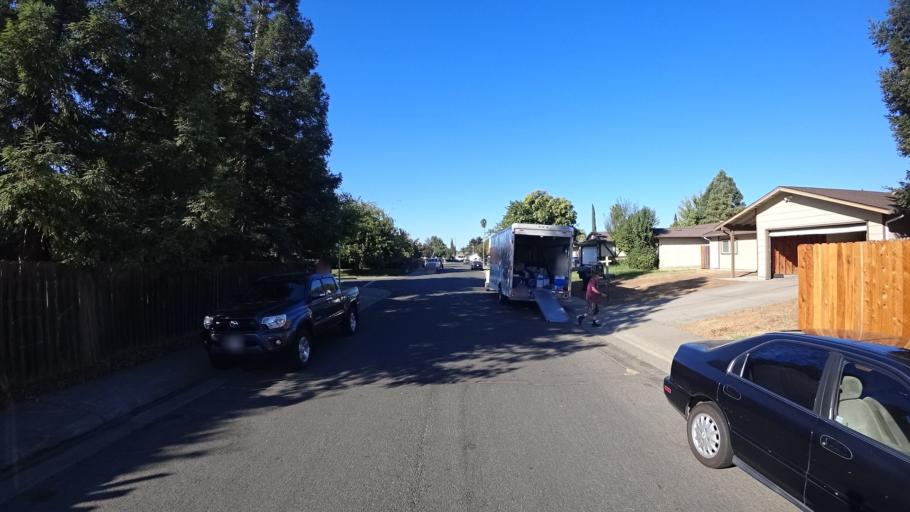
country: US
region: California
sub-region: Sacramento County
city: Laguna
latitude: 38.4546
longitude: -121.4421
